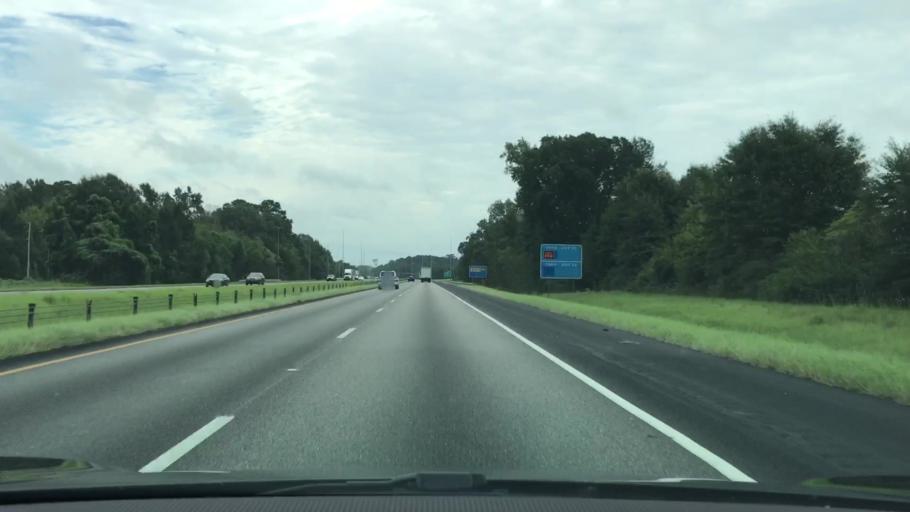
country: US
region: Alabama
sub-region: Elmore County
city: Tallassee
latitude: 32.4024
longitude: -85.9668
